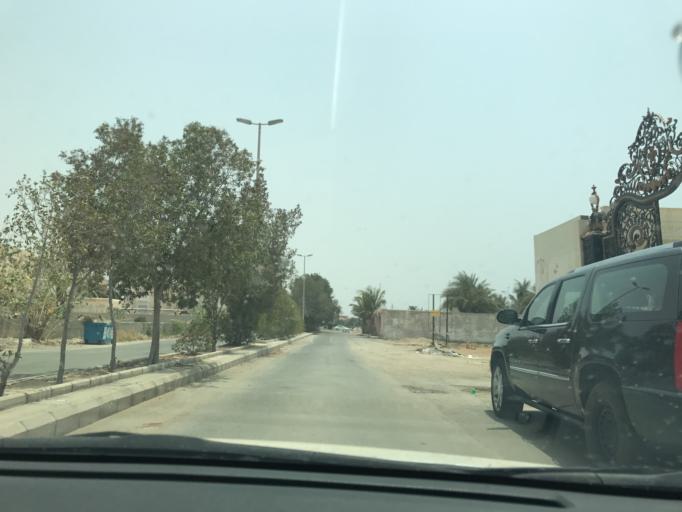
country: SA
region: Makkah
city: Jeddah
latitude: 21.6839
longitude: 39.1035
